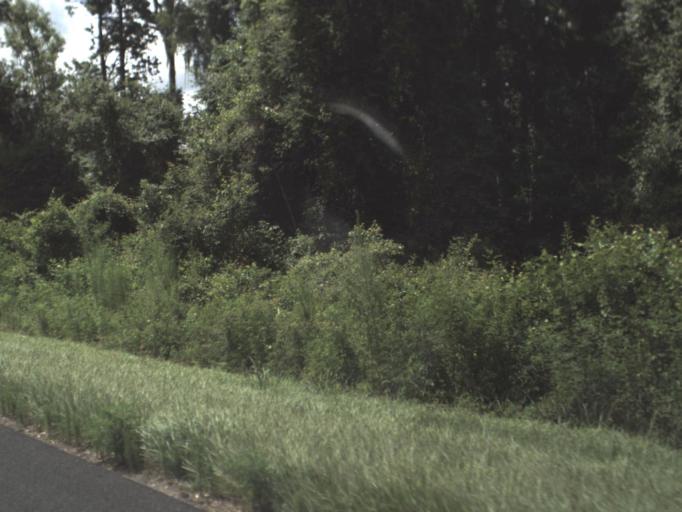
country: US
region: Florida
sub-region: Taylor County
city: Perry
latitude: 30.2854
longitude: -83.7320
